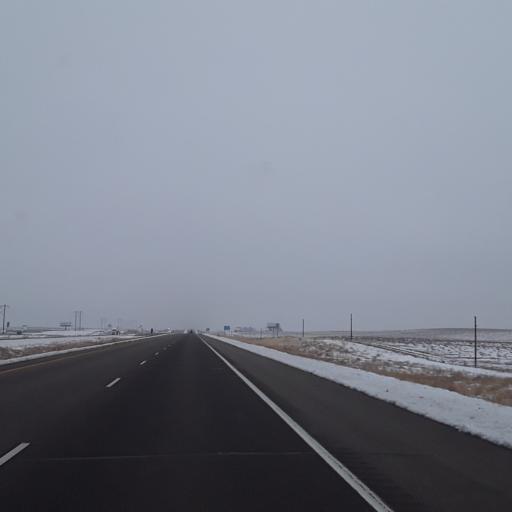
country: US
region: Colorado
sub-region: Logan County
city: Sterling
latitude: 40.4894
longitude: -103.2707
